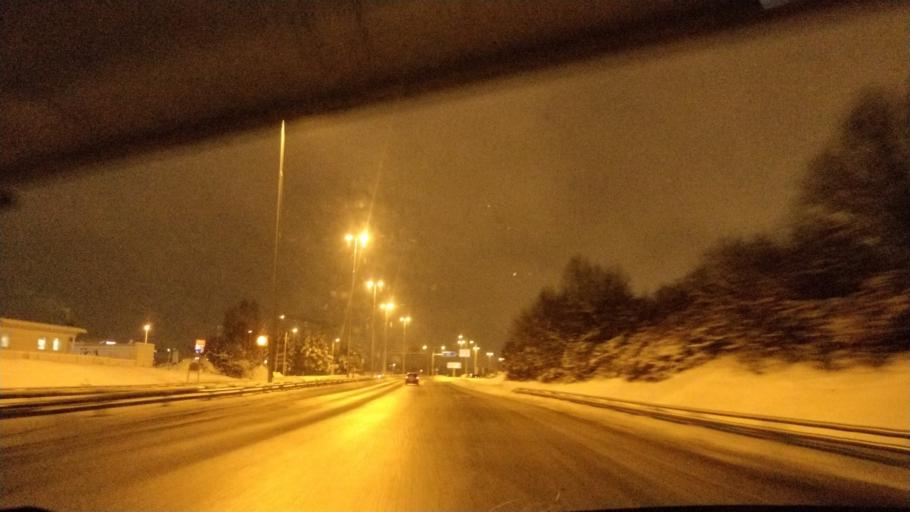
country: FI
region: Lapland
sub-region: Rovaniemi
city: Rovaniemi
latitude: 66.4992
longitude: 25.7171
